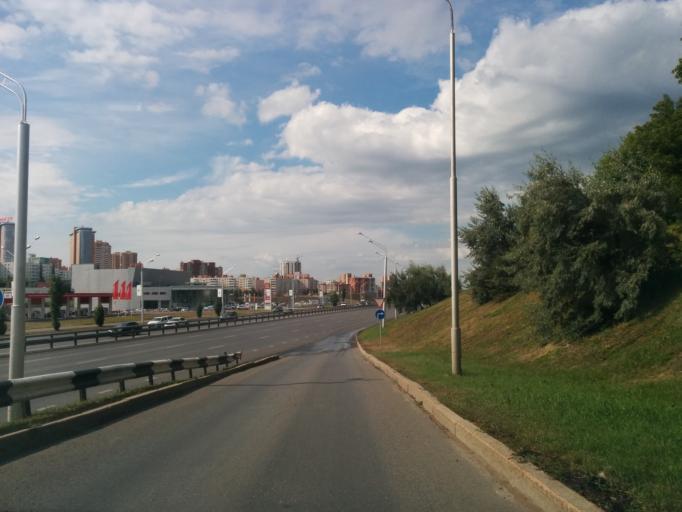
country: RU
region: Bashkortostan
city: Ufa
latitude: 54.7279
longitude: 55.9923
